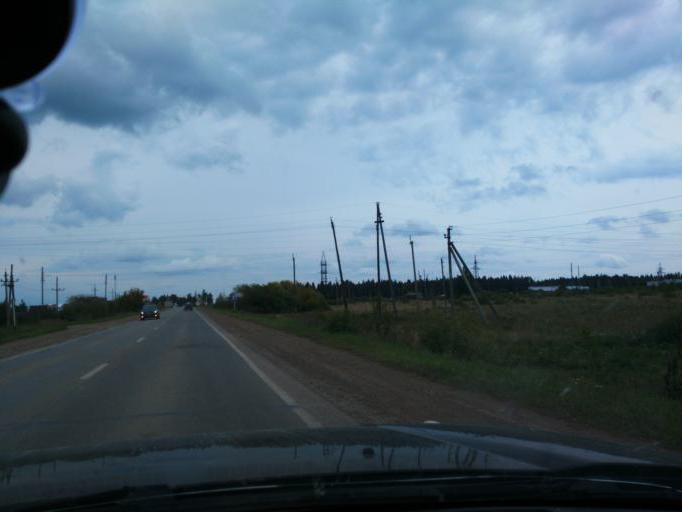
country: RU
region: Perm
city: Chernushka
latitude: 56.5327
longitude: 56.0847
